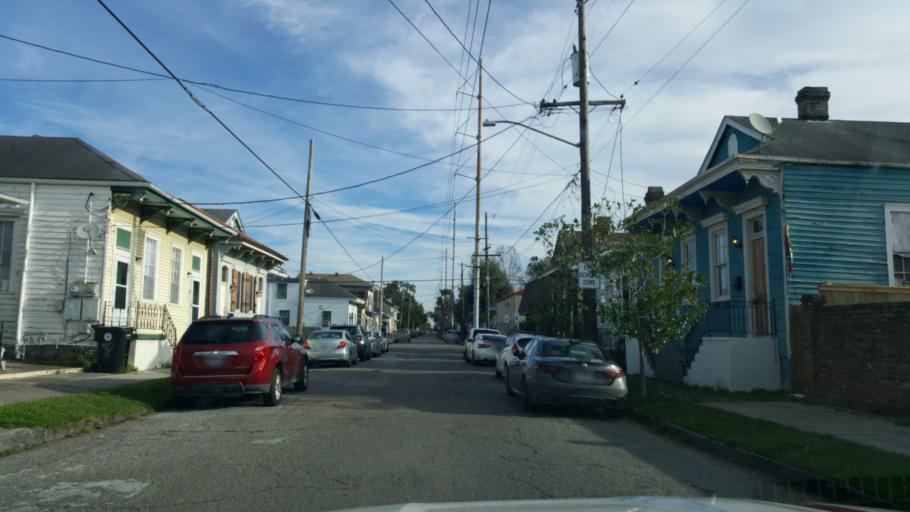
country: US
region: Louisiana
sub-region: Orleans Parish
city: New Orleans
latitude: 29.9693
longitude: -90.0731
